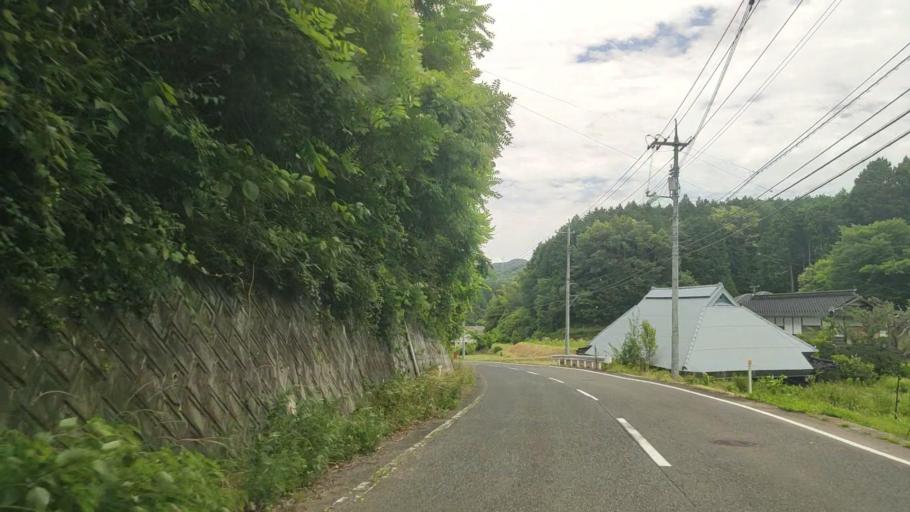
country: JP
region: Hyogo
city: Yamazakicho-nakabirose
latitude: 35.0954
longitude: 134.2916
